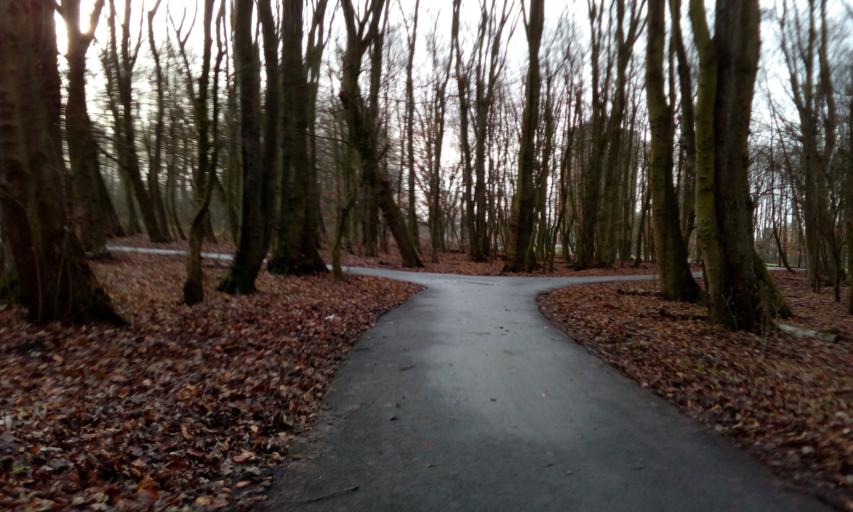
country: NL
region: South Holland
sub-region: Gemeente Lansingerland
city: Berkel en Rodenrijs
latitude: 51.9670
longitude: 4.4762
